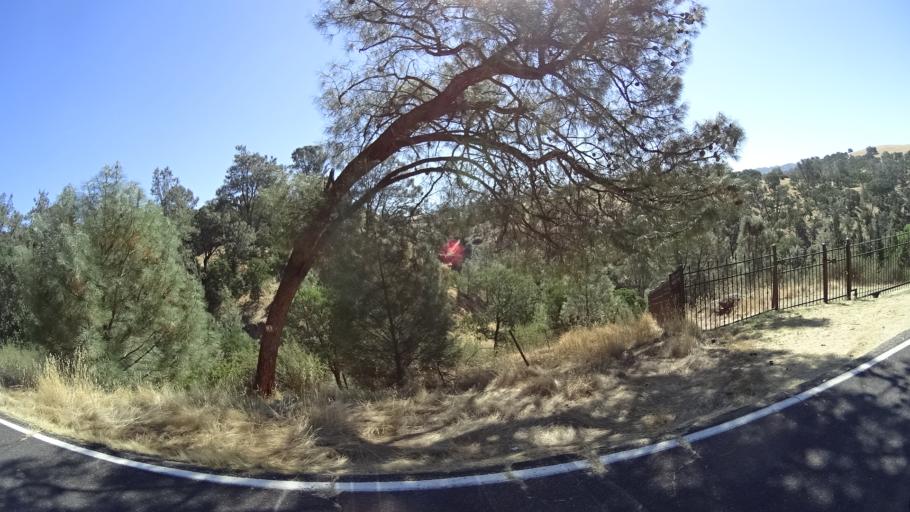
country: US
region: California
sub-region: Calaveras County
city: Rancho Calaveras
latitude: 38.0924
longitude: -120.8575
